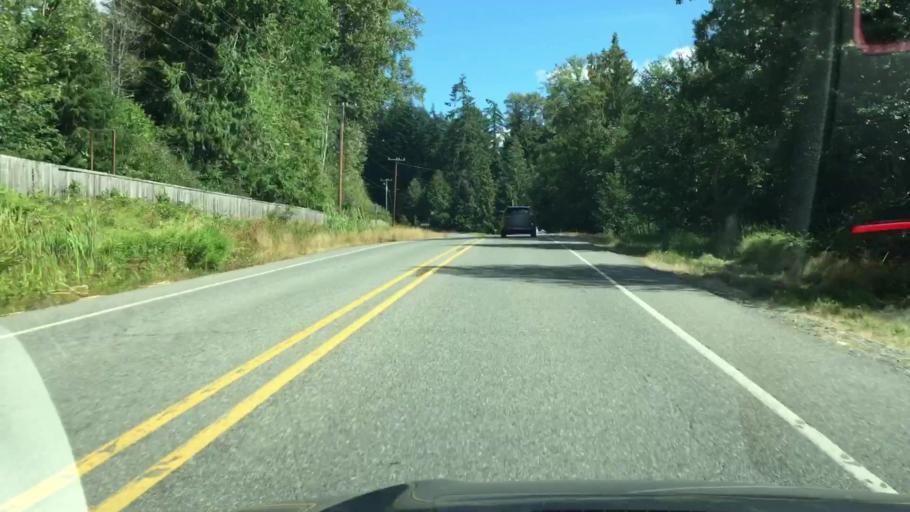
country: US
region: Washington
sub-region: Pierce County
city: Eatonville
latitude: 46.7574
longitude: -122.0258
